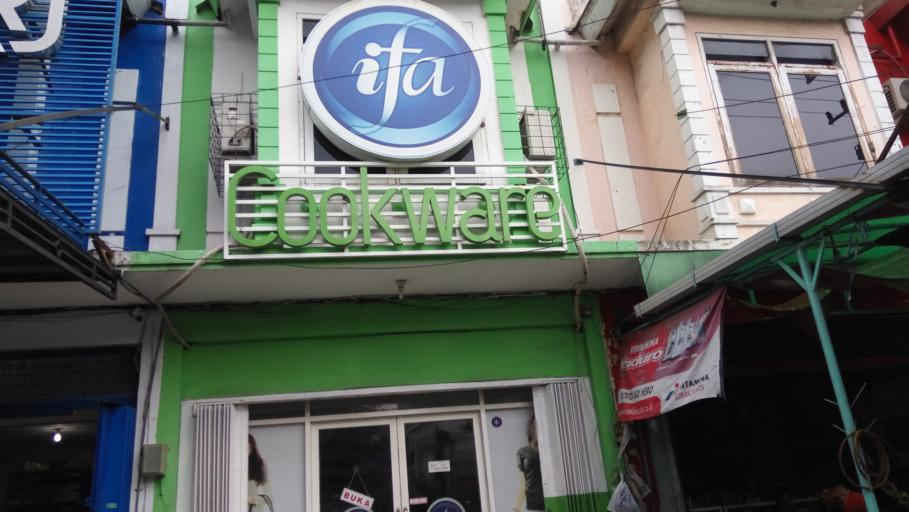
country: ID
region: East Java
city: Malang
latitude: -7.9602
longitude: 112.6136
